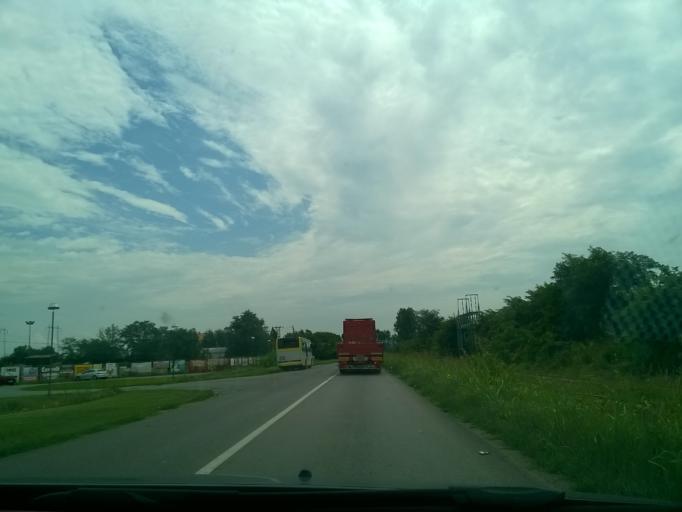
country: RS
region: Autonomna Pokrajina Vojvodina
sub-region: Srednjebanatski Okrug
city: Zrenjanin
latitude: 45.3864
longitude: 20.4244
